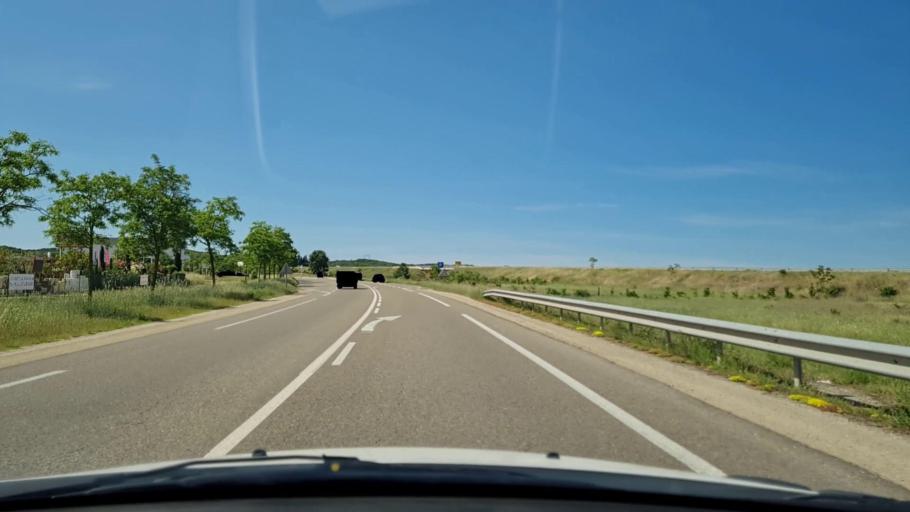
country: FR
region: Languedoc-Roussillon
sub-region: Departement du Gard
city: La Calmette
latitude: 43.9263
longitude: 4.2556
